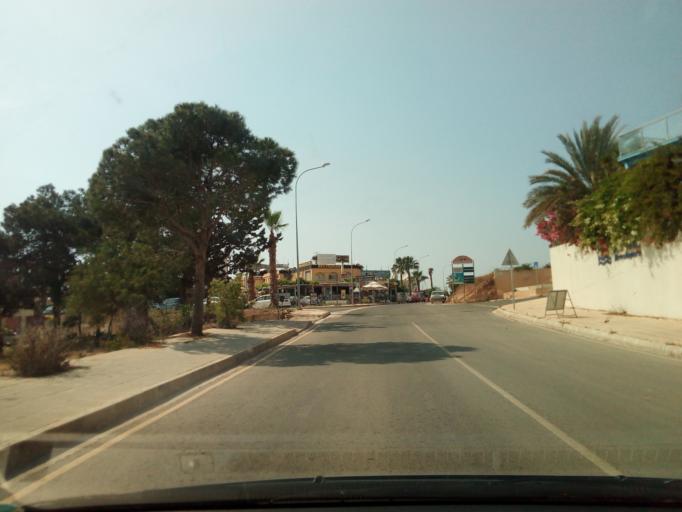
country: CY
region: Pafos
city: Pegeia
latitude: 34.8571
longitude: 32.3669
